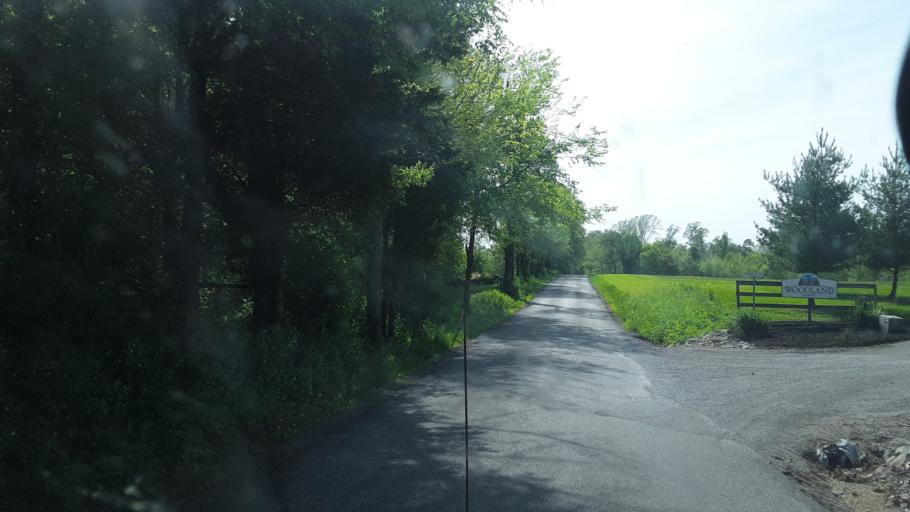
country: US
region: Illinois
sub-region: Jackson County
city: Carbondale
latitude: 37.6800
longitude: -89.2628
